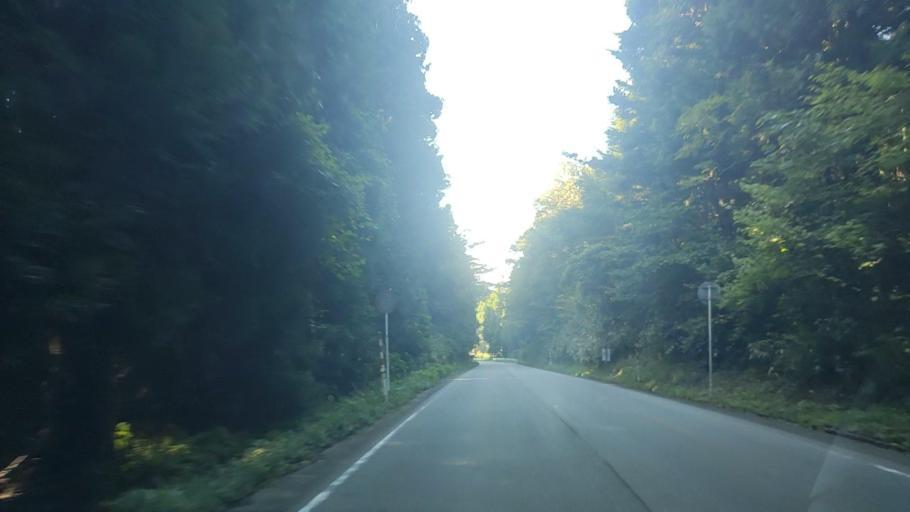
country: JP
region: Ishikawa
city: Nanao
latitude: 37.1226
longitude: 136.9352
